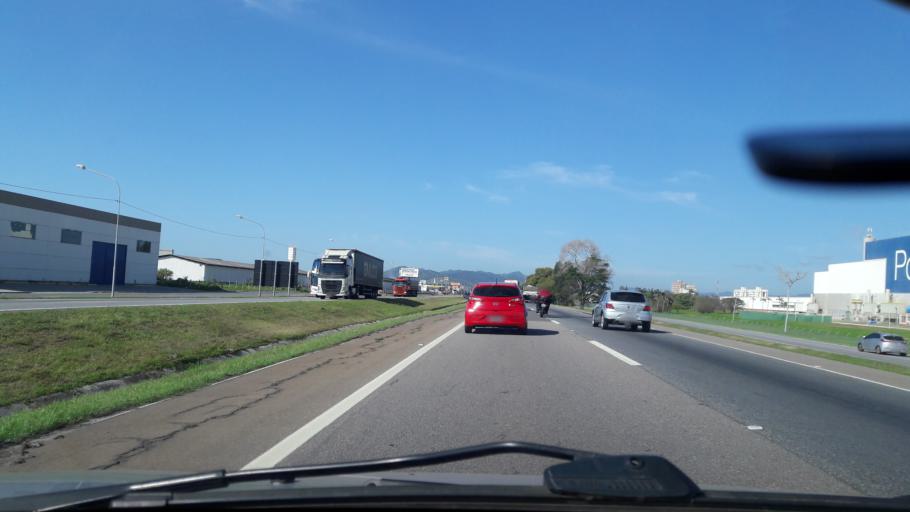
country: BR
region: Santa Catarina
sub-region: Tijucas
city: Tijucas
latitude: -27.2243
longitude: -48.6275
